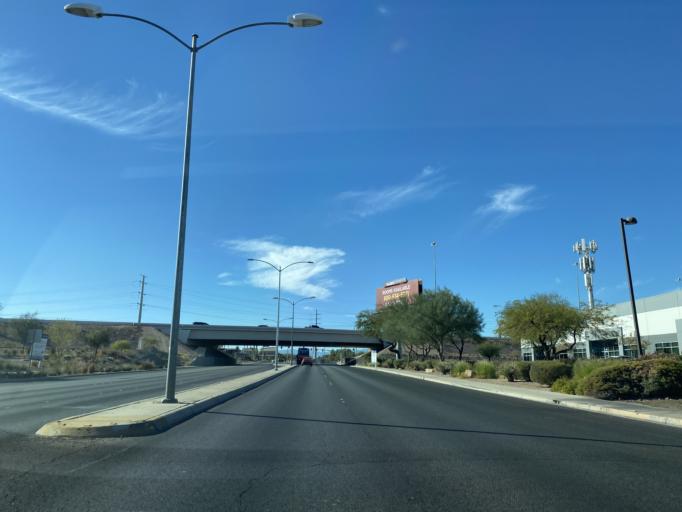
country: US
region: Nevada
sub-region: Clark County
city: Henderson
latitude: 36.0564
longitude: -115.0256
